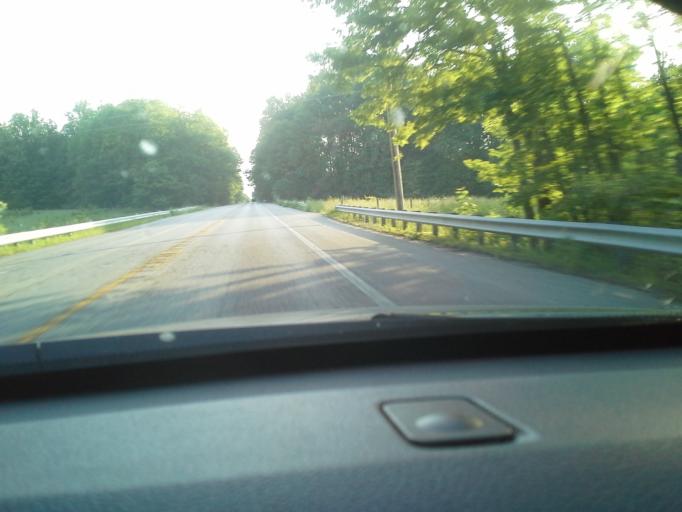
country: US
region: Maryland
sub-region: Anne Arundel County
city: Deale
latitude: 38.7890
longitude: -76.5862
